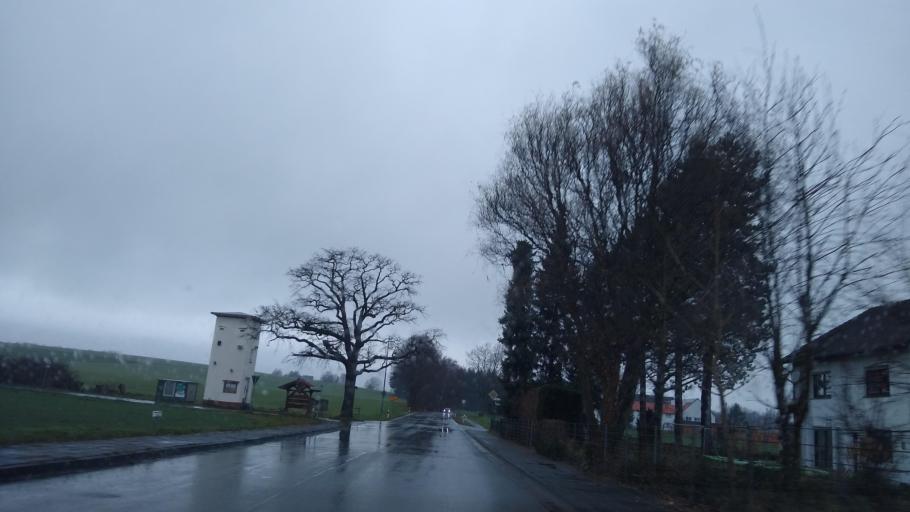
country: DE
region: North Rhine-Westphalia
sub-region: Regierungsbezirk Detmold
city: Lugde
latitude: 51.9138
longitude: 9.2823
